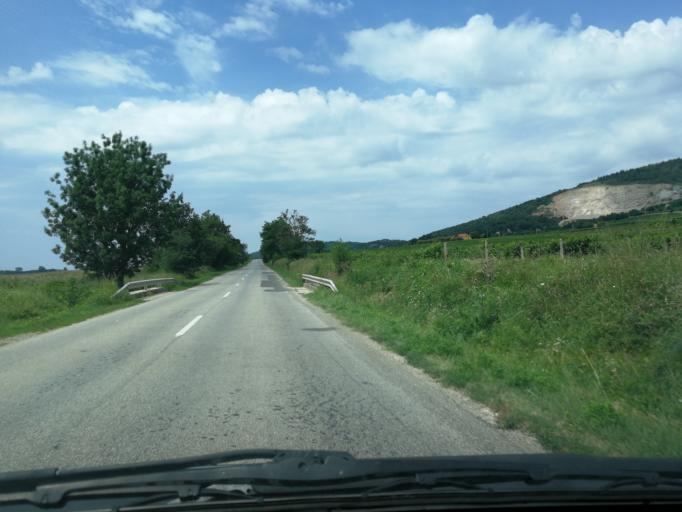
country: HU
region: Baranya
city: Harkany
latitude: 45.8732
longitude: 18.2610
